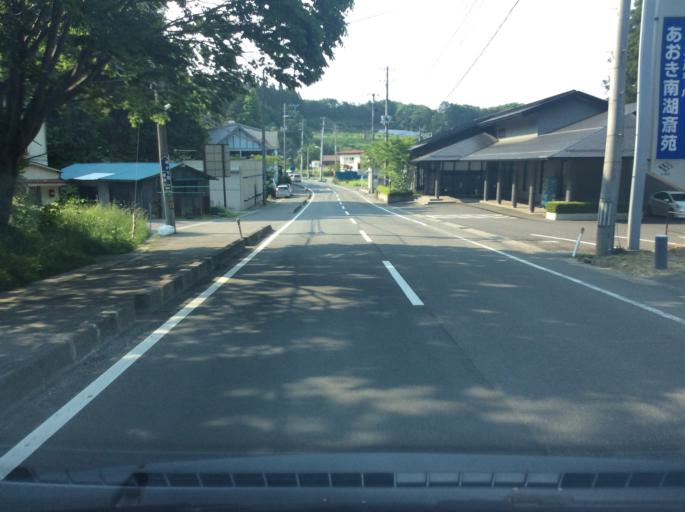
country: JP
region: Fukushima
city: Ishikawa
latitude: 37.1125
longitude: 140.2274
